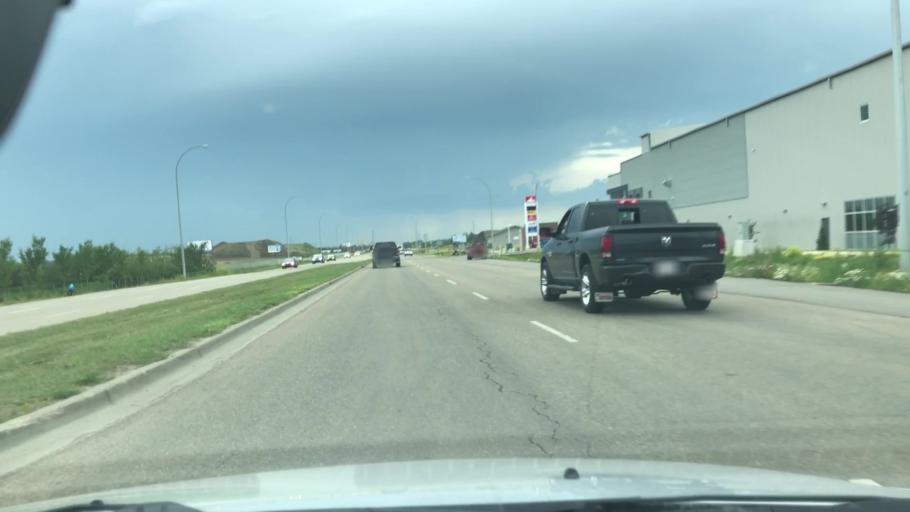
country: CA
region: Alberta
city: St. Albert
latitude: 53.5994
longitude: -113.6030
